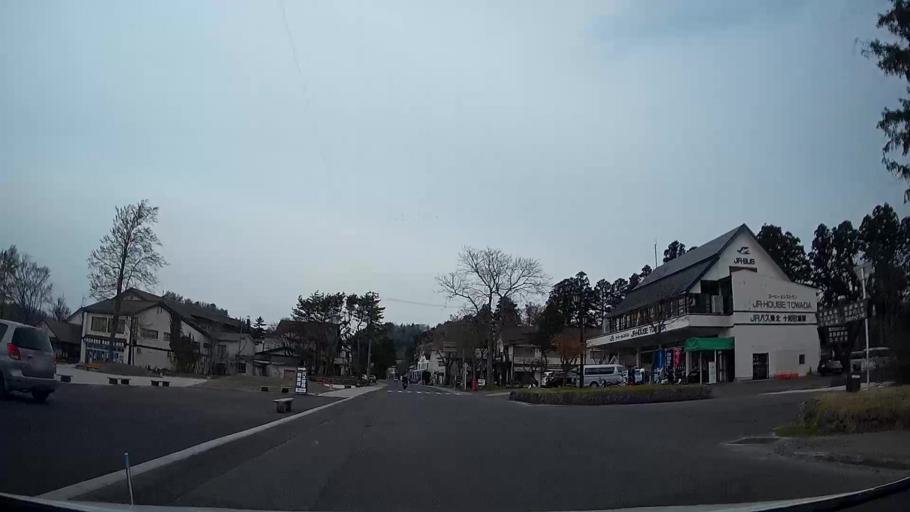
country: JP
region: Akita
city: Hanawa
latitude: 40.4262
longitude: 140.8940
